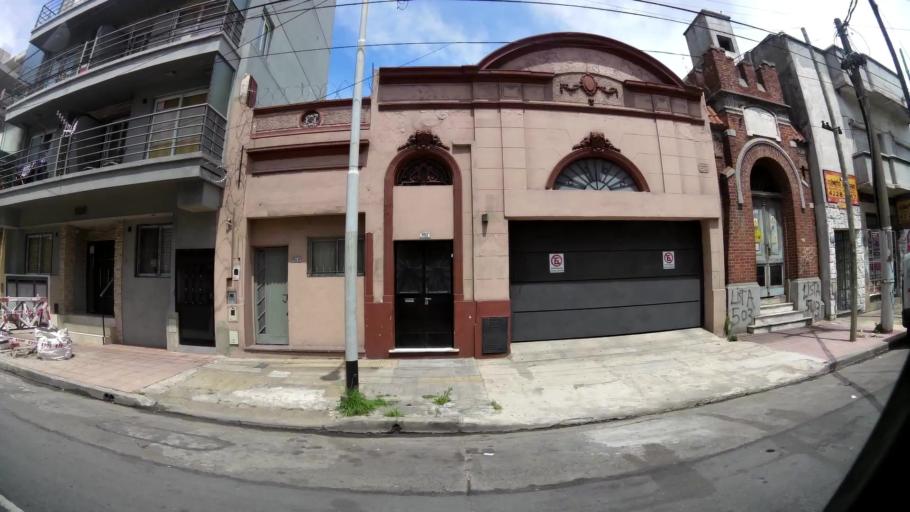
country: AR
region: Buenos Aires
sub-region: Partido de Avellaneda
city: Avellaneda
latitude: -34.6706
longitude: -58.3921
